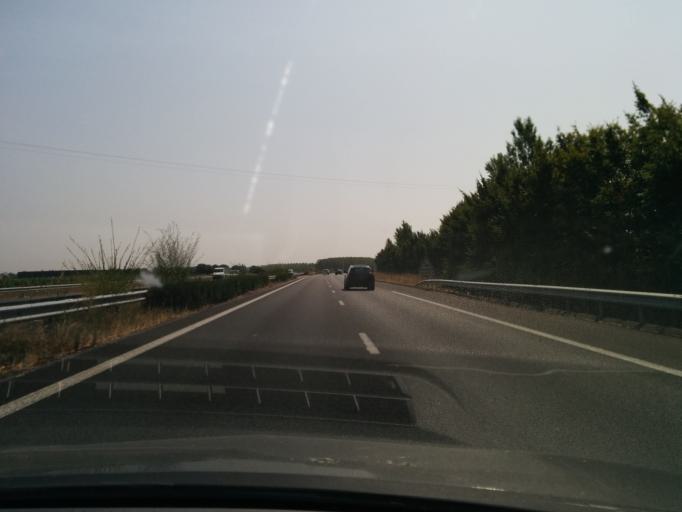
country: FR
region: Midi-Pyrenees
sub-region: Departement du Tarn
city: Lagrave
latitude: 43.8888
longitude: 1.9711
